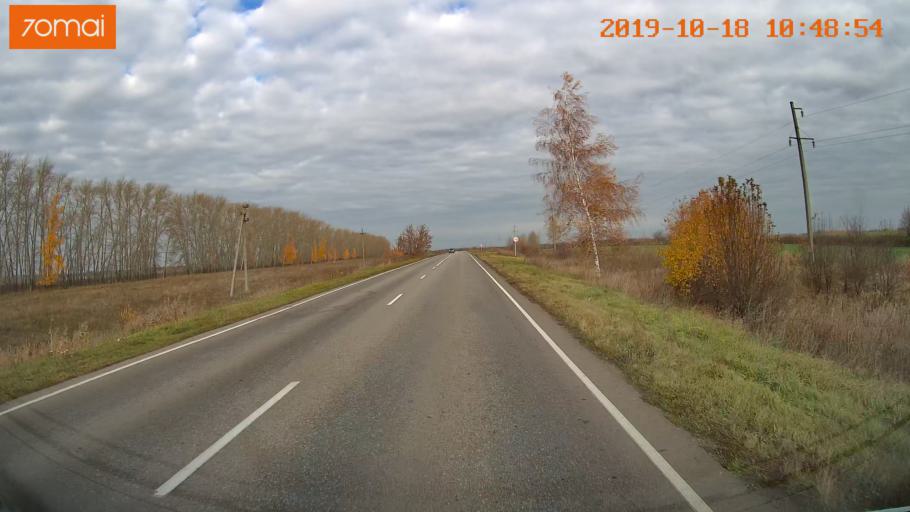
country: RU
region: Tula
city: Yepifan'
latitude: 53.7238
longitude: 38.6971
